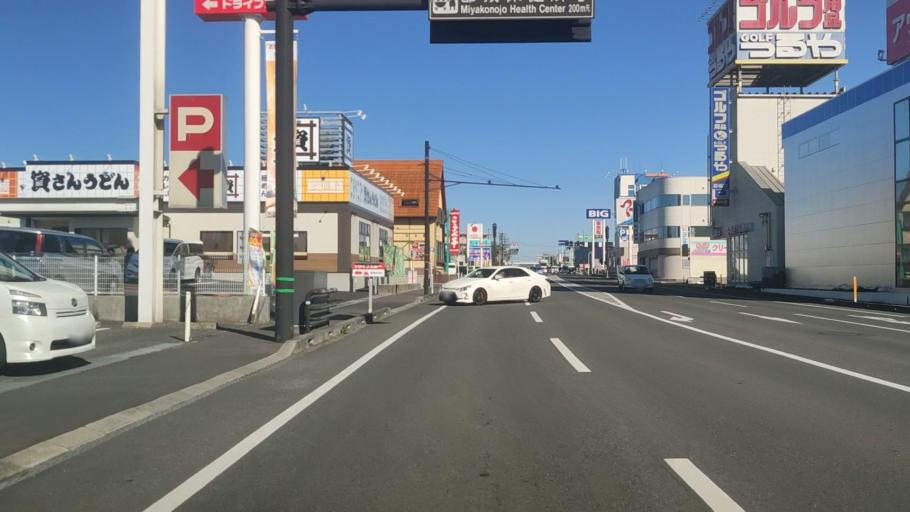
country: JP
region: Miyazaki
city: Miyakonojo
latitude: 31.7388
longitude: 131.0705
